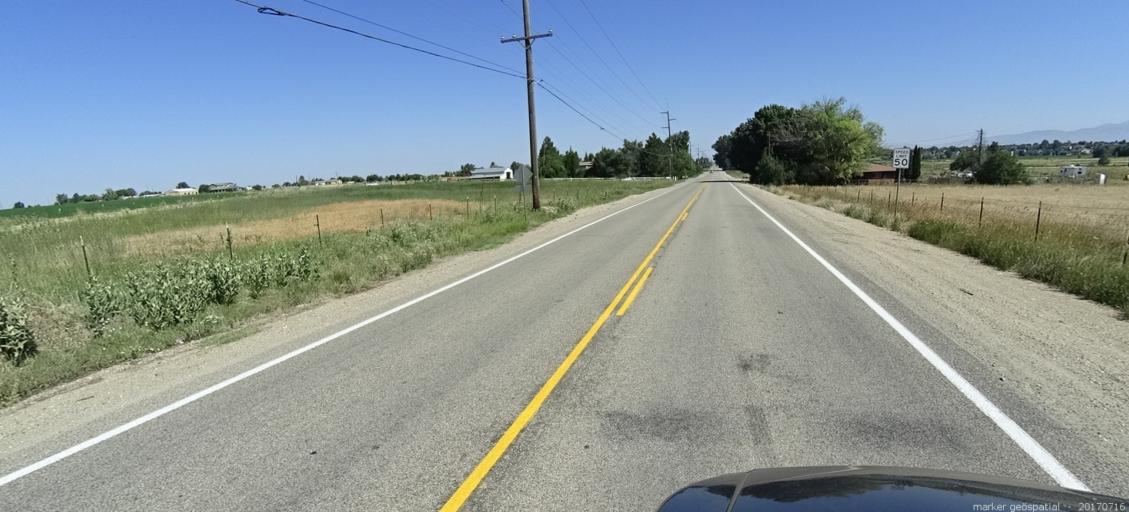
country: US
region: Idaho
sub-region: Ada County
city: Kuna
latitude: 43.5187
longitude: -116.3345
